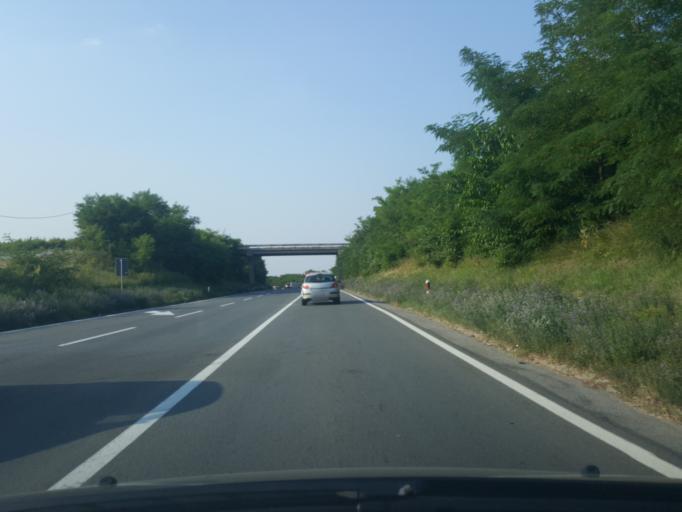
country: RS
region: Central Serbia
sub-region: Belgrade
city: Sopot
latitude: 44.5374
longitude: 20.6580
